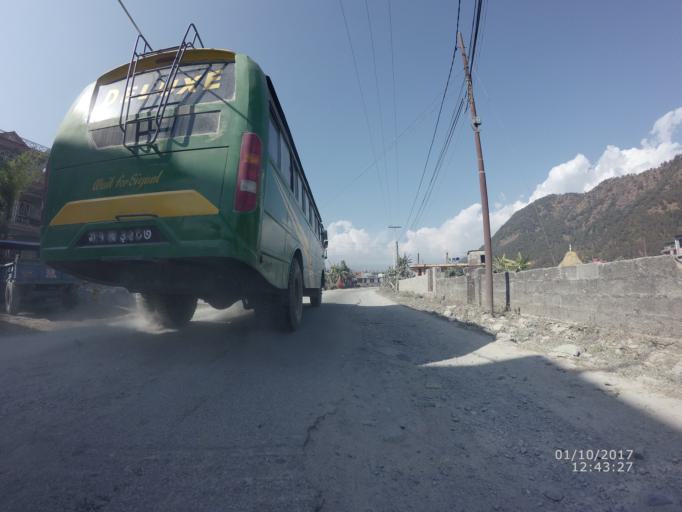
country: NP
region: Western Region
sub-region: Gandaki Zone
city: Pokhara
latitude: 28.2671
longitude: 83.9652
